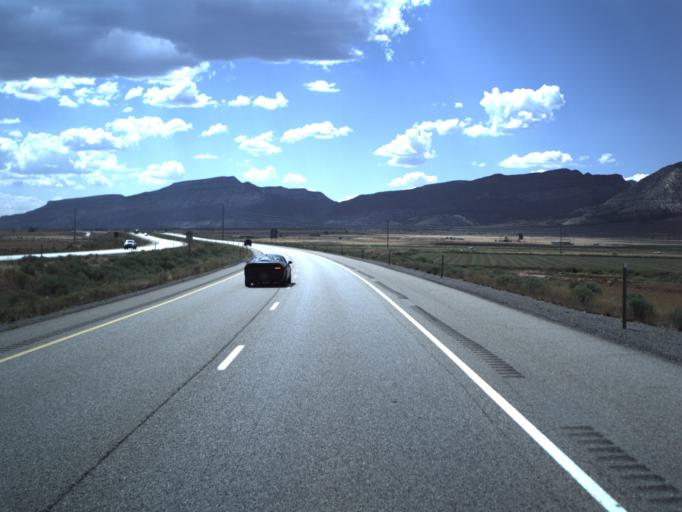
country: US
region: Utah
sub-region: Sevier County
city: Aurora
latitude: 38.8796
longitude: -111.9482
